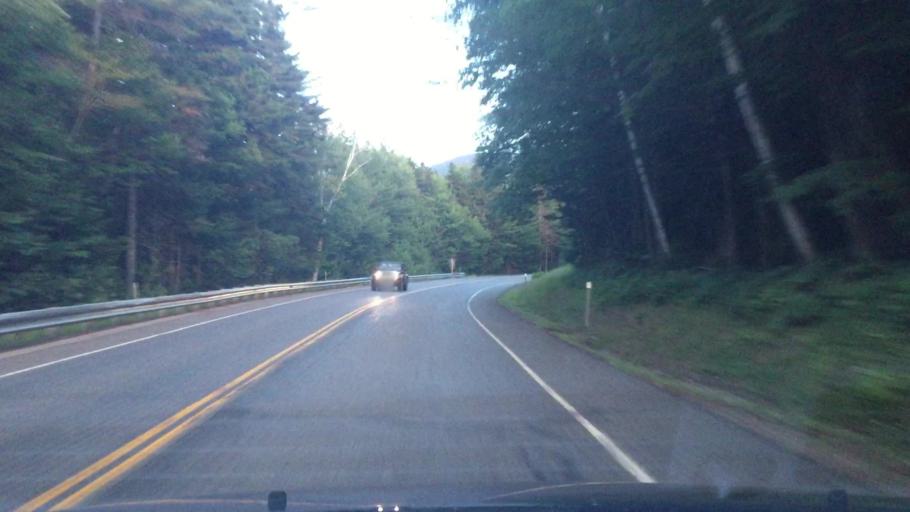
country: US
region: New Hampshire
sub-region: Grafton County
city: Woodstock
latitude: 44.0352
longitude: -71.5288
